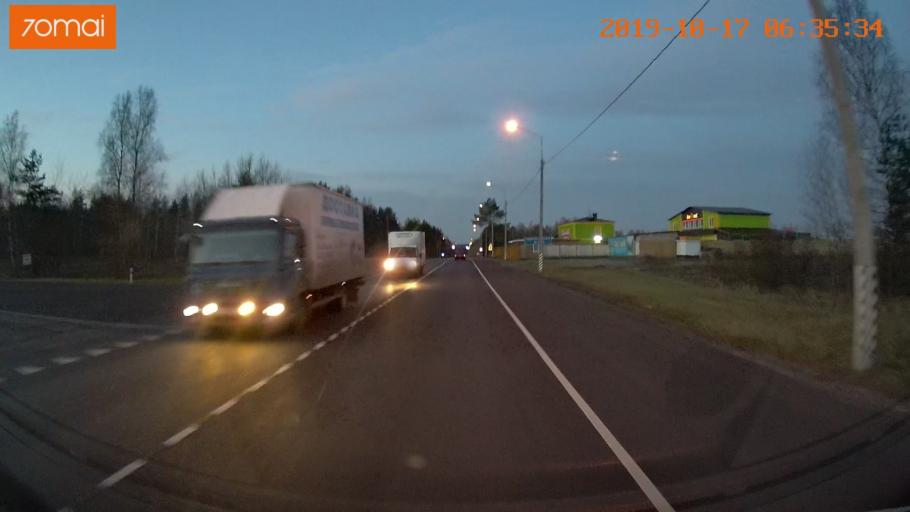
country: RU
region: Ivanovo
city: Novoye Leushino
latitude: 56.6909
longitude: 40.6194
